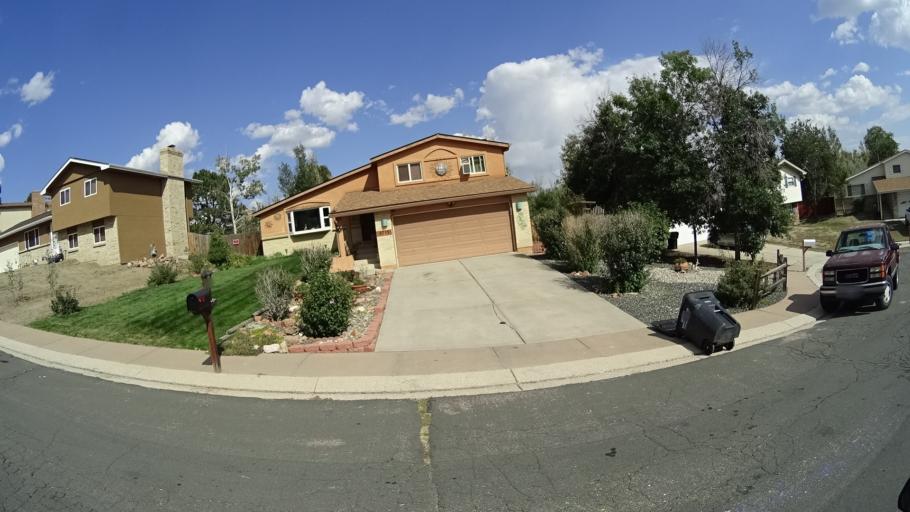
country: US
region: Colorado
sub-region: El Paso County
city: Cimarron Hills
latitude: 38.8715
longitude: -104.7241
